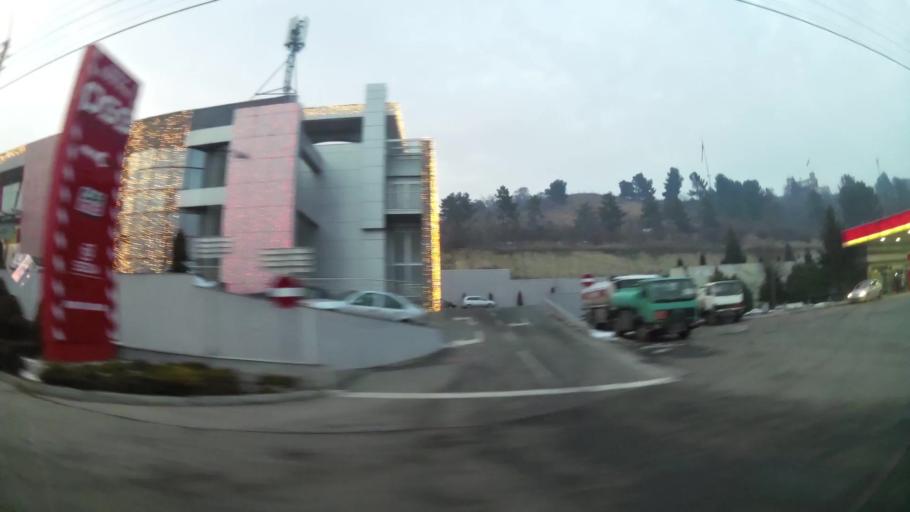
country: MK
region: Suto Orizari
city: Suto Orizare
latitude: 42.0150
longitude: 21.3990
